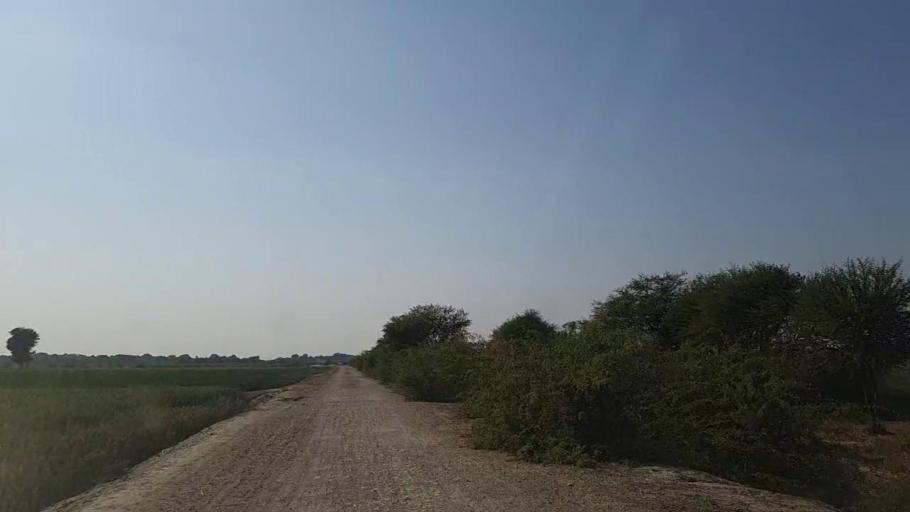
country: PK
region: Sindh
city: Naukot
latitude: 24.9310
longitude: 69.4862
